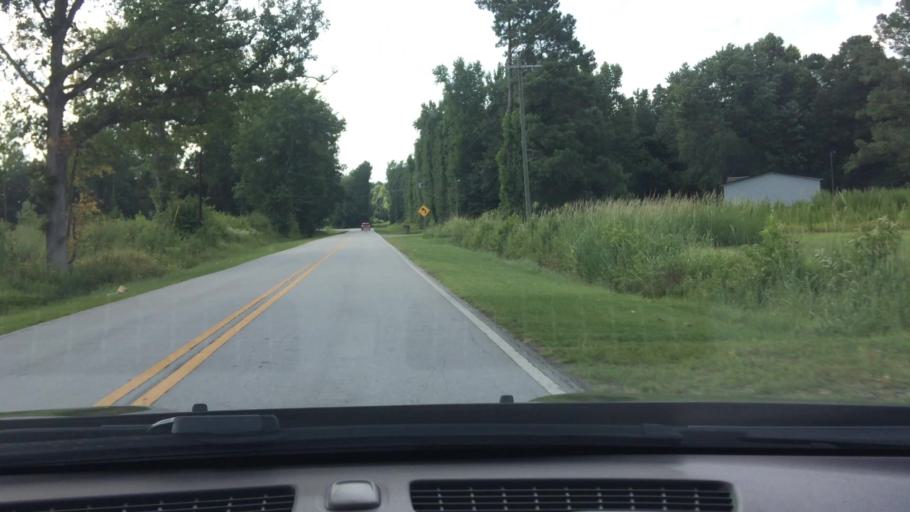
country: US
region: North Carolina
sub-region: Beaufort County
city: River Road
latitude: 35.4335
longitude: -76.9829
